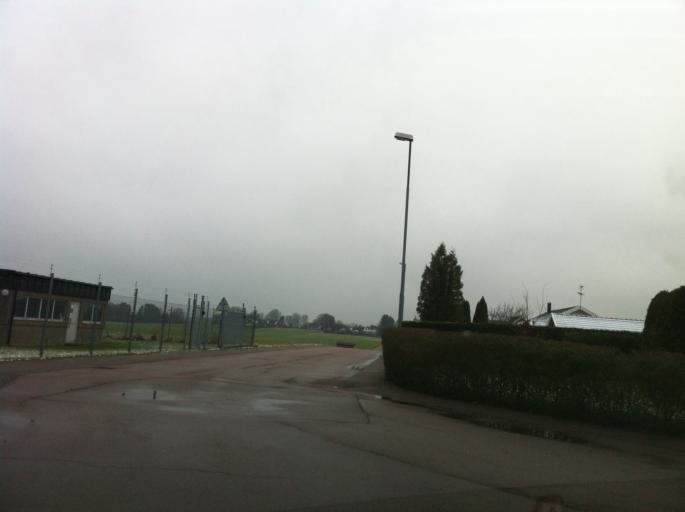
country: SE
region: Skane
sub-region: Bjuvs Kommun
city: Billesholm
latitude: 55.9937
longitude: 12.9652
